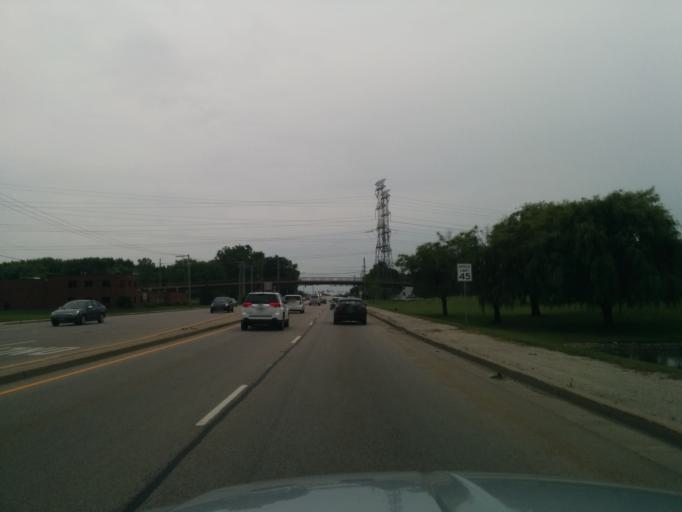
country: US
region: Illinois
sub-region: DuPage County
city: Warrenville
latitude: 41.7972
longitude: -88.2408
